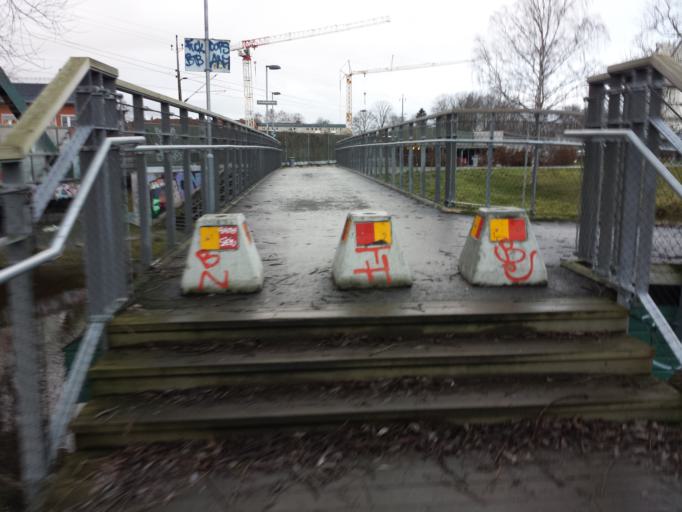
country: SE
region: Uppsala
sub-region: Uppsala Kommun
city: Uppsala
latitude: 59.8668
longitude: 17.6268
